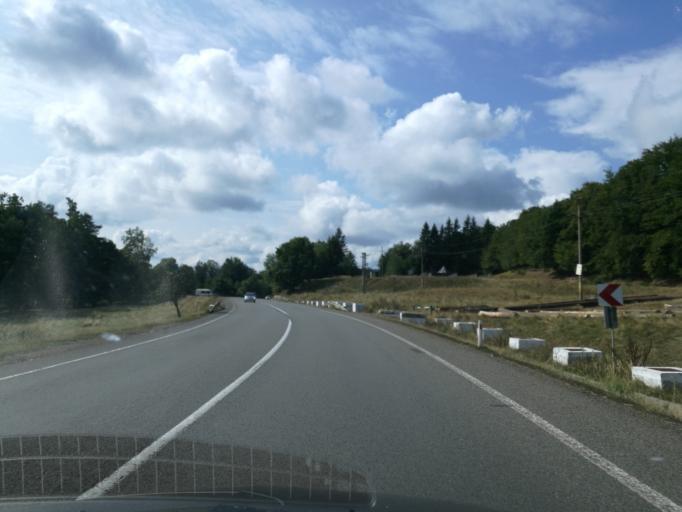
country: RO
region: Suceava
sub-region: Comuna Ilisesti
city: Ilisesti
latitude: 47.5918
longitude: 26.0202
